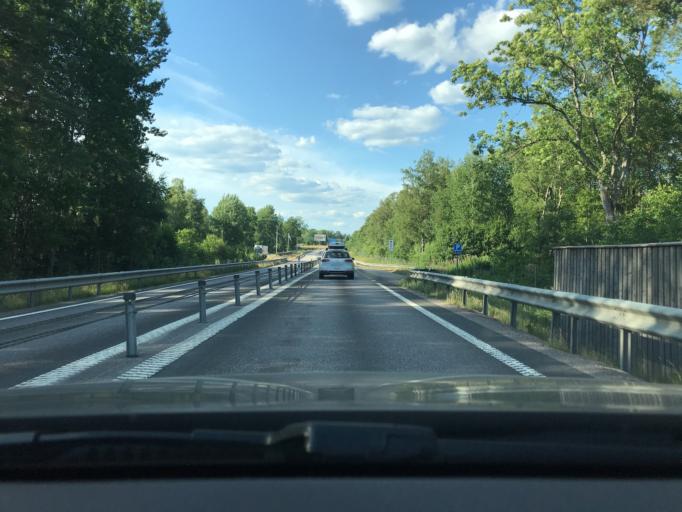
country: SE
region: Kronoberg
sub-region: Vaxjo Kommun
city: Rottne
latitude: 56.9762
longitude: 14.9810
